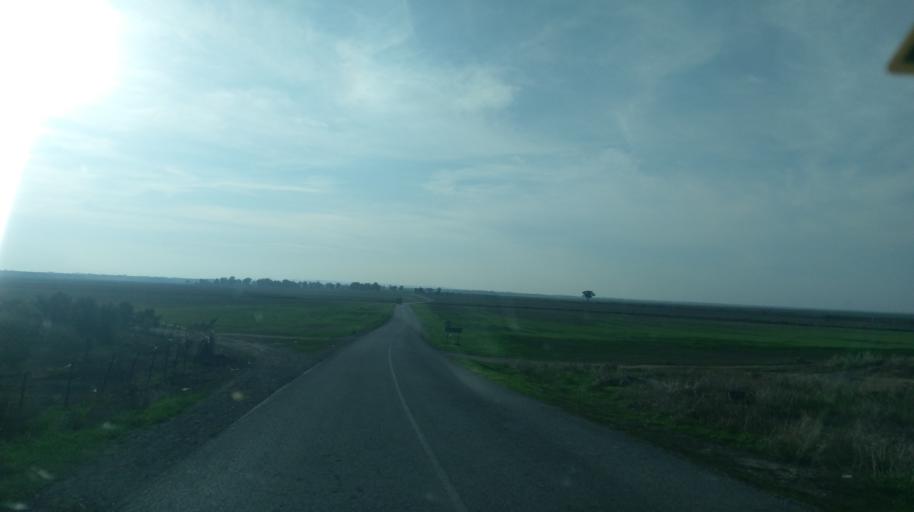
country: CY
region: Ammochostos
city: Acheritou
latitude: 35.0992
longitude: 33.8592
